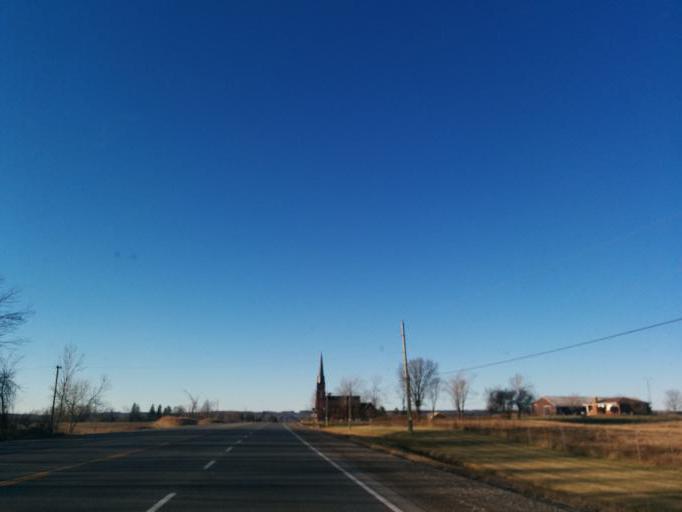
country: CA
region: Ontario
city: Brampton
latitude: 43.7947
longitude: -79.9069
